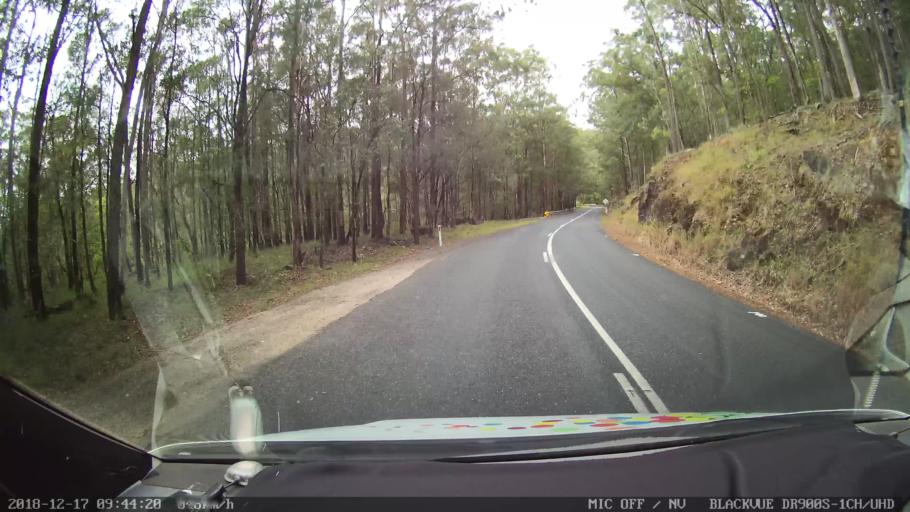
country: AU
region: New South Wales
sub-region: Tenterfield Municipality
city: Carrolls Creek
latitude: -28.9253
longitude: 152.3245
